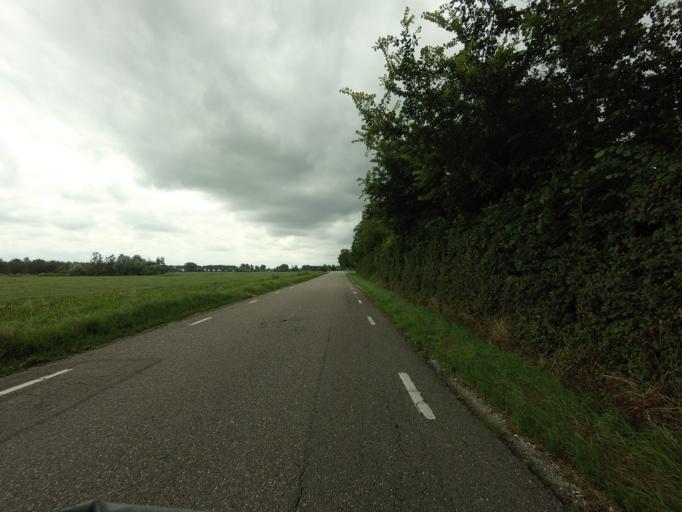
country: NL
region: South Holland
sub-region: Gemeente Giessenlanden
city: Giessenburg
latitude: 51.8978
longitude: 4.9016
